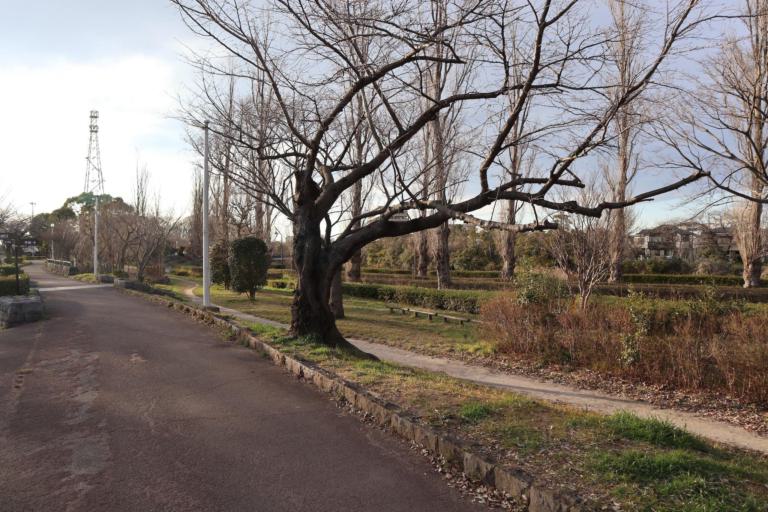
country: JP
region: Chiba
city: Matsudo
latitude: 35.7940
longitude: 139.8644
